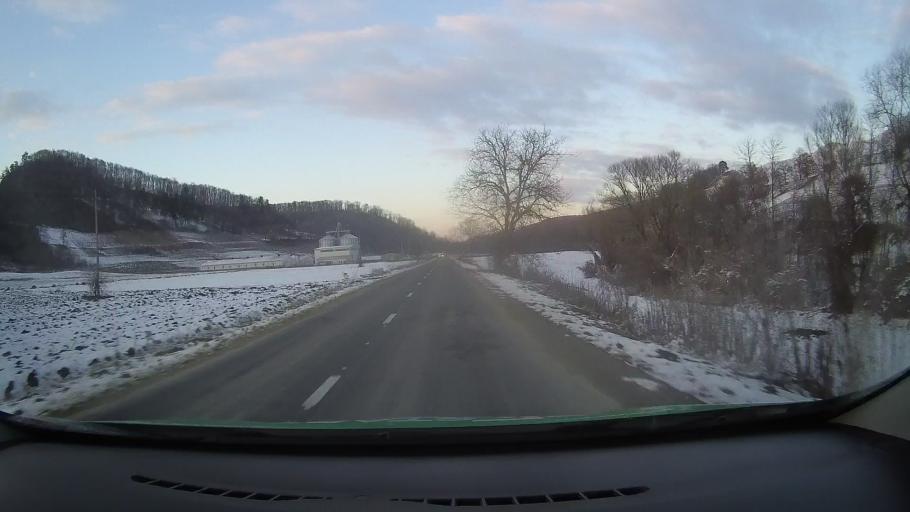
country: RO
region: Sibiu
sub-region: Comuna Atel
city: Atel
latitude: 46.1672
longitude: 24.4669
